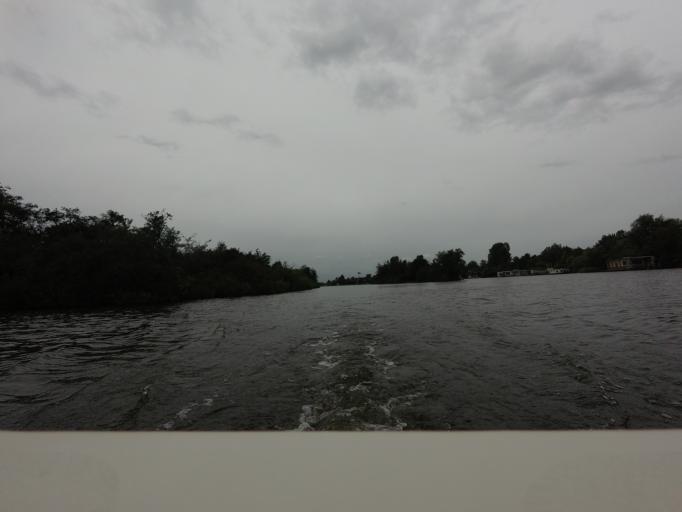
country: NL
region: Friesland
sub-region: Gemeente Tytsjerksteradiel
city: Garyp
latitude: 53.1214
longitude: 5.9433
